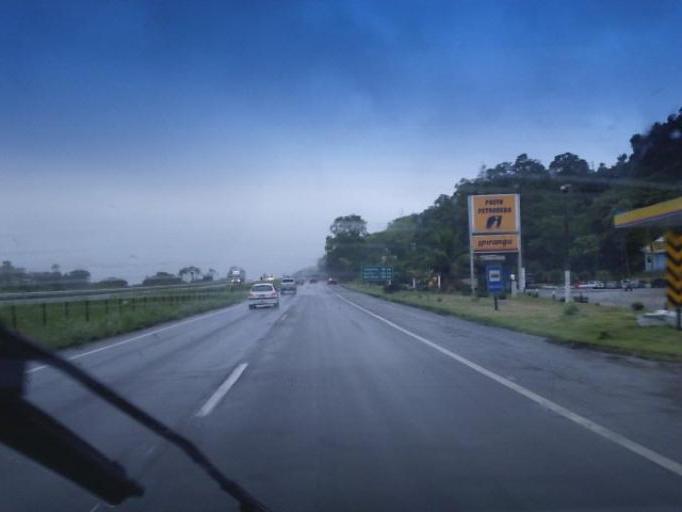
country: BR
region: Sao Paulo
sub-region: Miracatu
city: Miracatu
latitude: -24.2859
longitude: -47.4435
